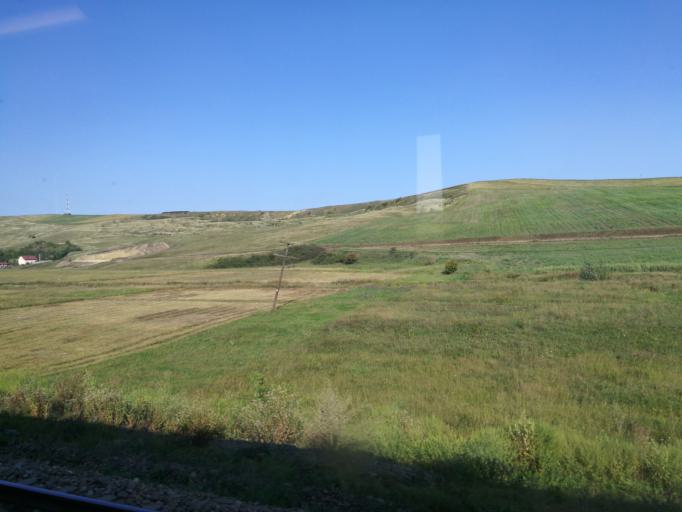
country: RO
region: Vaslui
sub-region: Comuna Rebricea
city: Rebricea
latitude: 46.8689
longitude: 27.5654
